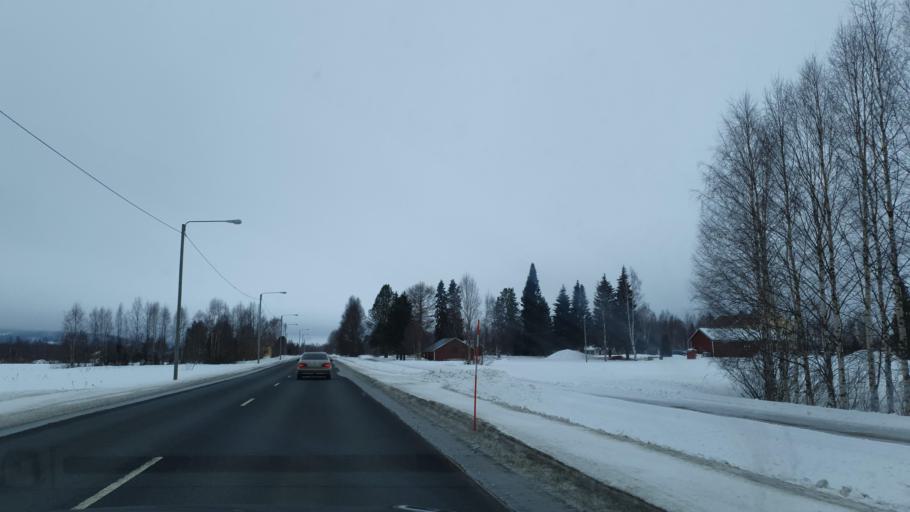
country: FI
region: Lapland
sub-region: Torniolaakso
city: Pello
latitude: 66.5728
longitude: 23.8801
